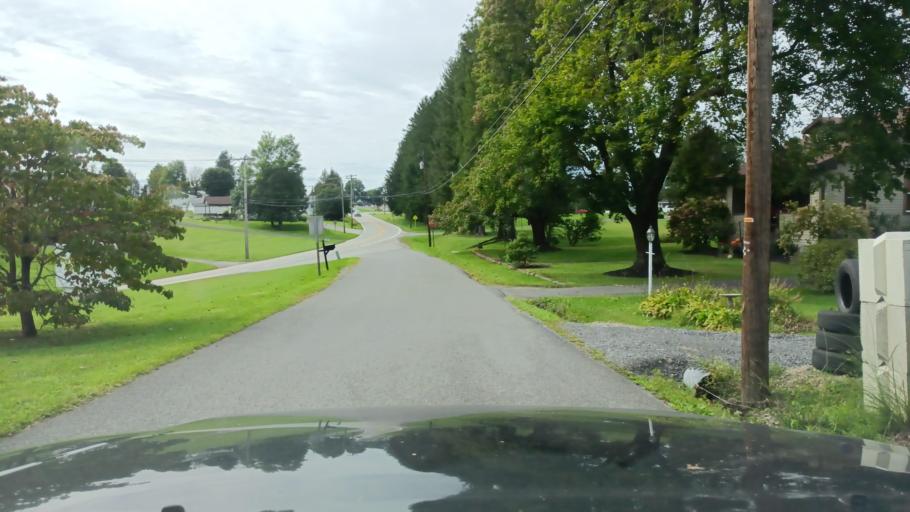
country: US
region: West Virginia
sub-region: Taylor County
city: Grafton
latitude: 39.3484
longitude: -80.0153
